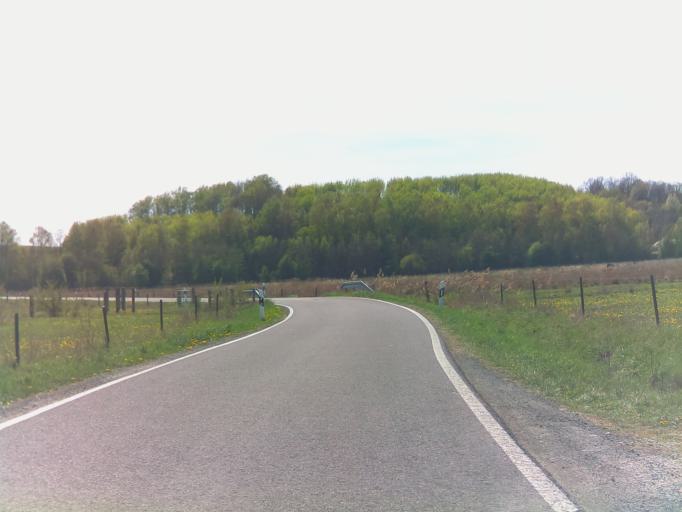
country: DE
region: Thuringia
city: Veilsdorf
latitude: 50.3286
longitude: 10.7987
